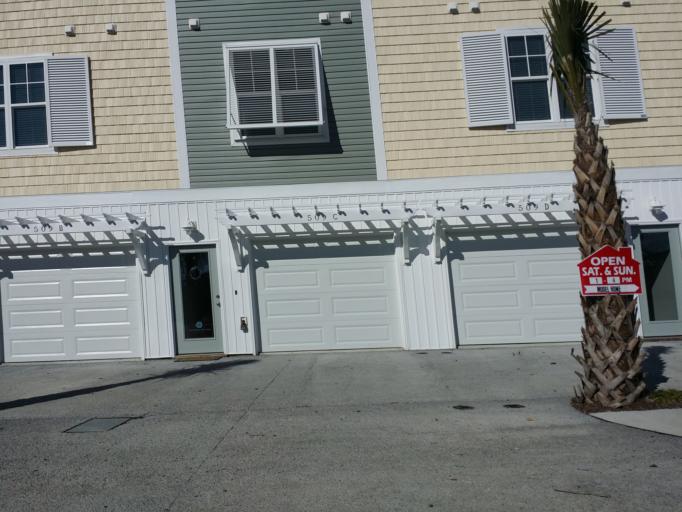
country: US
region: North Carolina
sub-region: Pender County
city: Surf City
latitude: 34.4318
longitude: -77.5374
